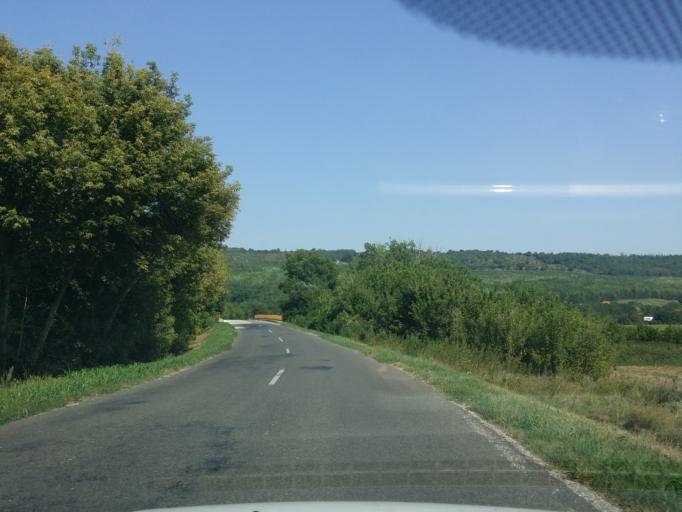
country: HU
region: Tolna
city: Gyonk
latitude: 46.5982
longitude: 18.4181
